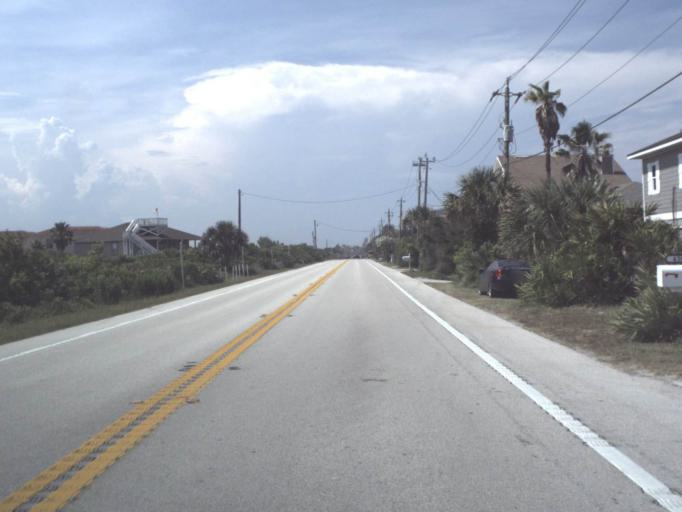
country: US
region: Florida
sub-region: Saint Johns County
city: Villano Beach
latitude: 29.9565
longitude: -81.3059
